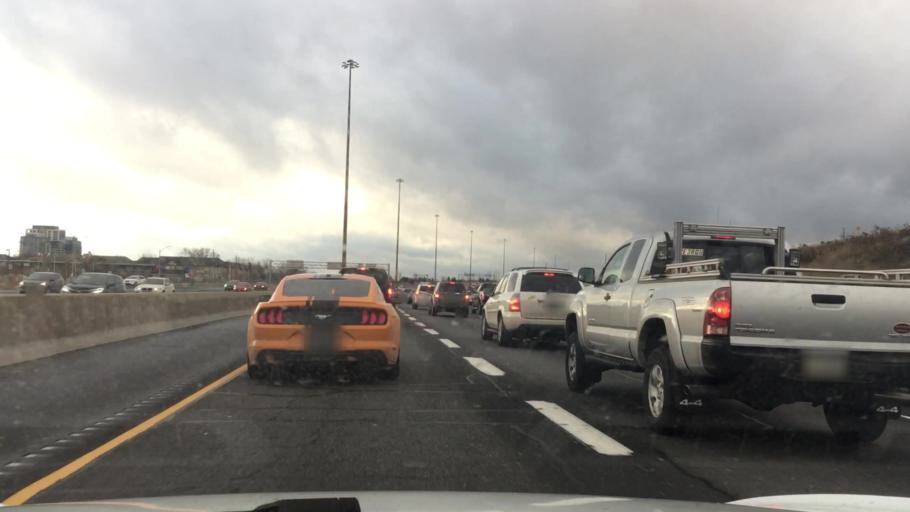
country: CA
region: Ontario
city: Burlington
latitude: 43.3510
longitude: -79.8059
